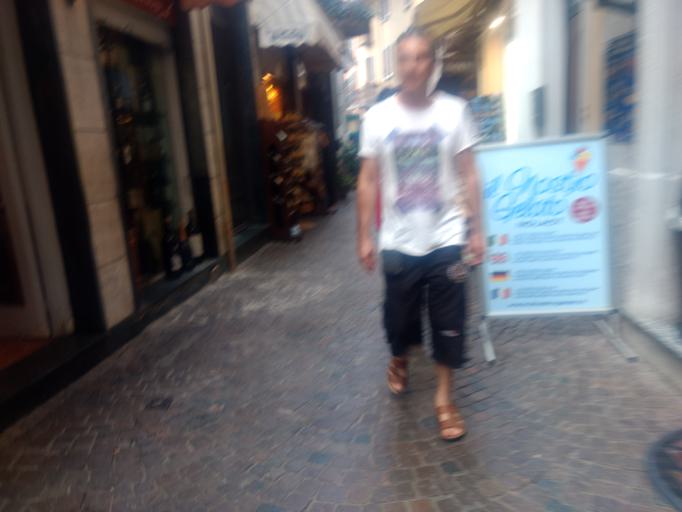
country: IT
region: Piedmont
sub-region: Provincia Verbano-Cusio-Ossola
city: Stresa
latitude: 45.8836
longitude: 8.5407
